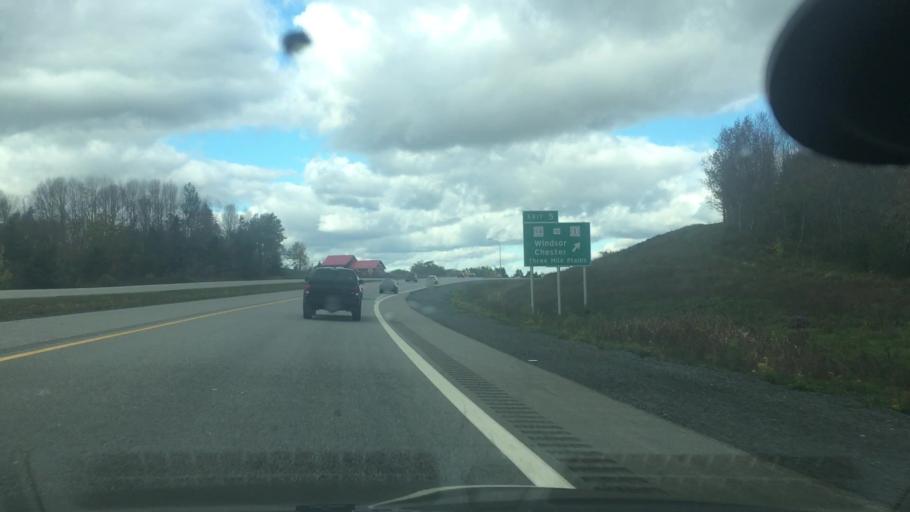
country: CA
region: Nova Scotia
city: Windsor
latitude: 44.9686
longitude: -64.0930
